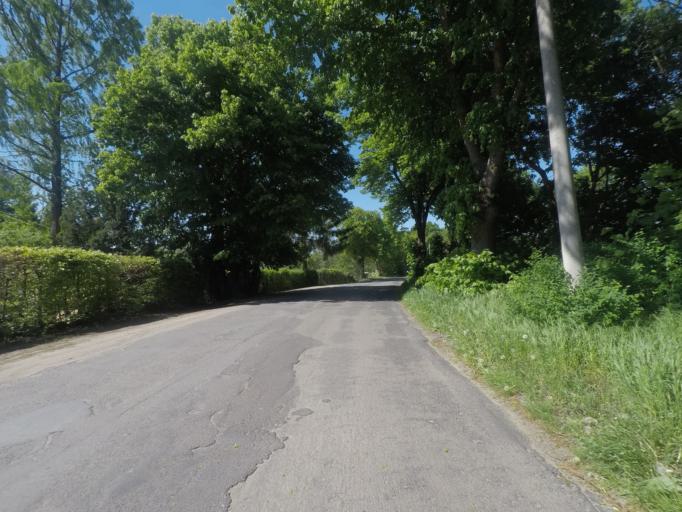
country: DE
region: Brandenburg
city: Melchow
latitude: 52.8476
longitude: 13.7176
